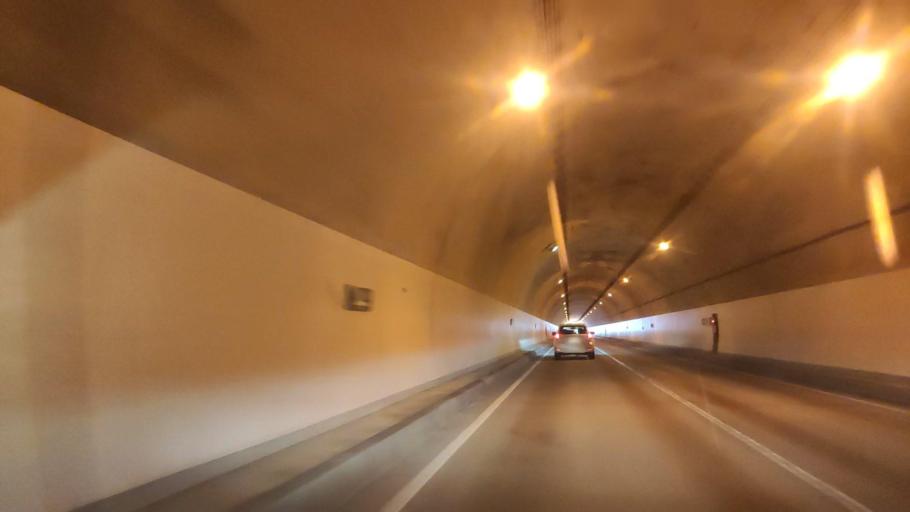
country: JP
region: Hokkaido
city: Ishikari
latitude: 43.4743
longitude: 141.3954
